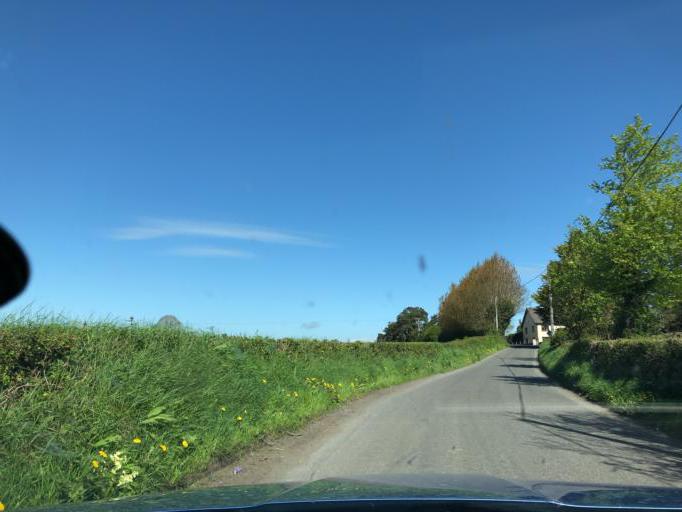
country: IE
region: Connaught
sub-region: County Galway
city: Portumna
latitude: 53.1506
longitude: -8.2928
